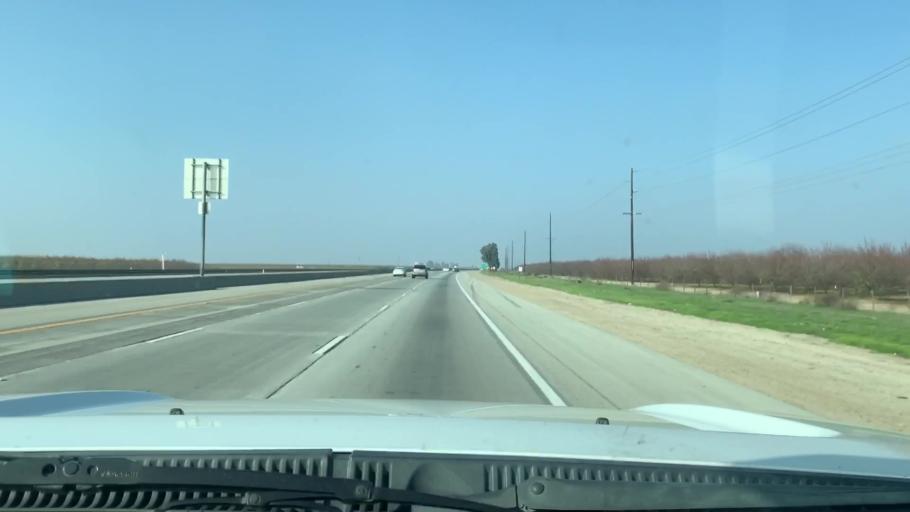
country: US
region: California
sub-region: Kern County
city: Shafter
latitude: 35.5095
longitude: -119.1761
